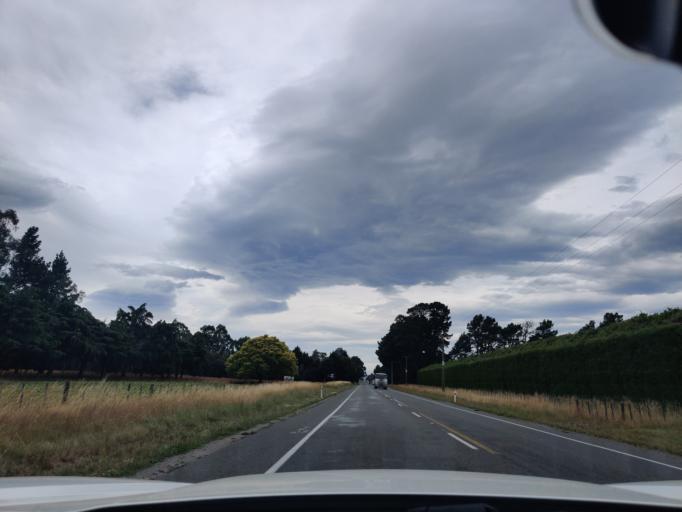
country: NZ
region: Wellington
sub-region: Masterton District
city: Masterton
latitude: -40.9870
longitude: 175.5763
